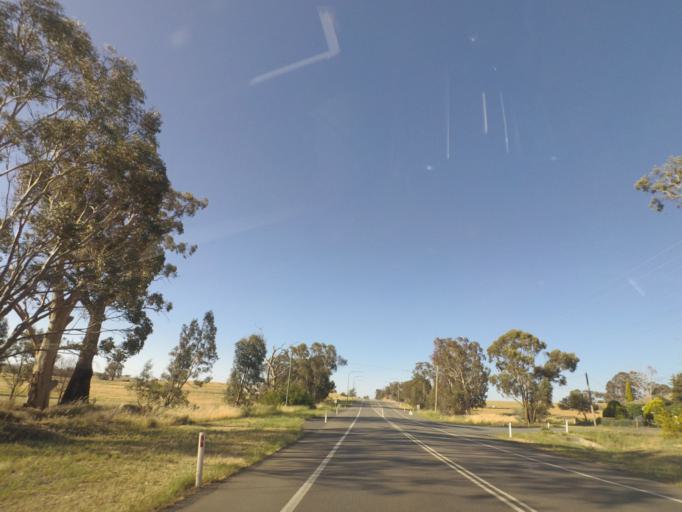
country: AU
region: New South Wales
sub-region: Wagga Wagga
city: Forest Hill
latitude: -35.2693
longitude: 147.7451
